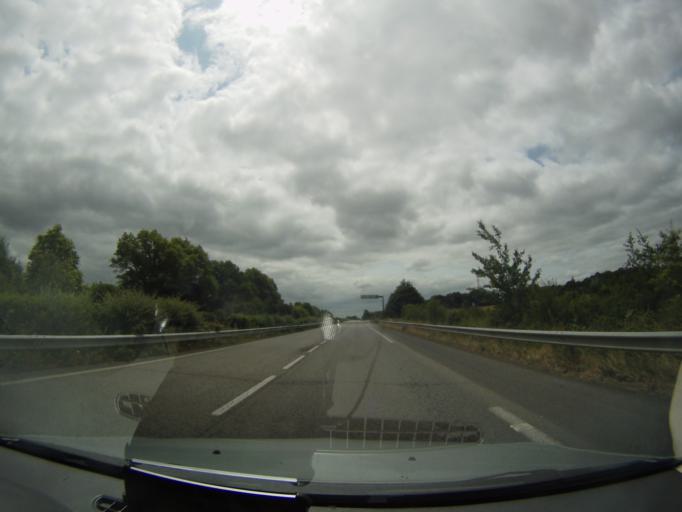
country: FR
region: Pays de la Loire
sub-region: Departement de la Loire-Atlantique
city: Nozay
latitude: 47.5395
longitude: -1.6362
